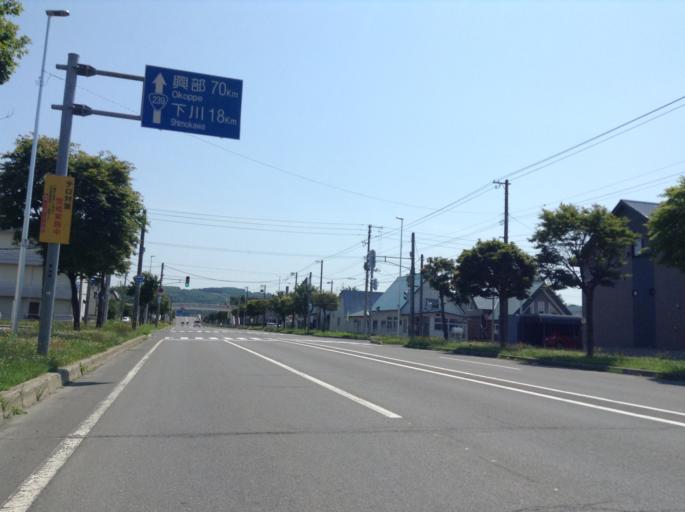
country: JP
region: Hokkaido
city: Nayoro
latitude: 44.3564
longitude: 142.4581
